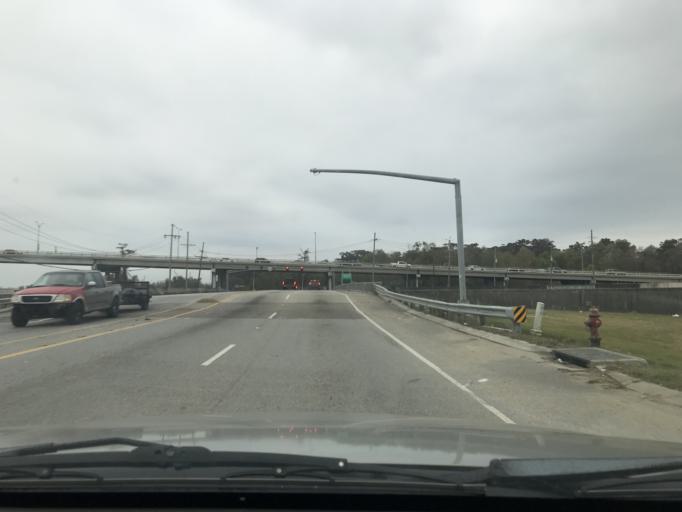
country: US
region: Louisiana
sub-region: Jefferson Parish
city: Woodmere
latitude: 29.8719
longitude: -90.0725
